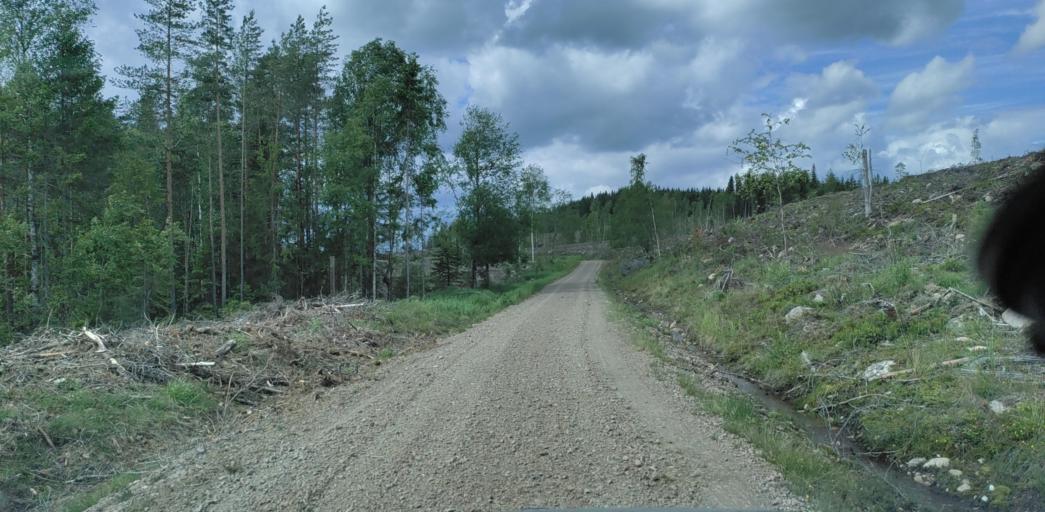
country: SE
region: Vaermland
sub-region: Munkfors Kommun
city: Munkfors
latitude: 59.9477
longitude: 13.4196
